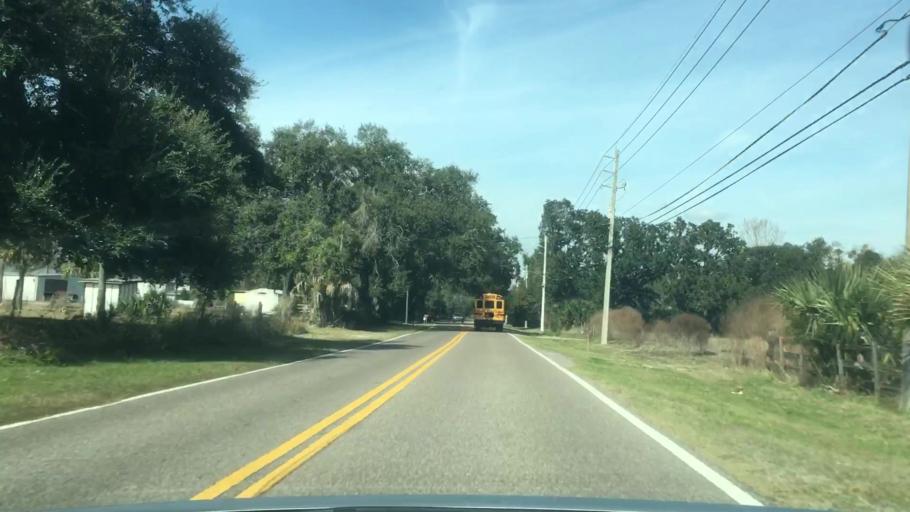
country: US
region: Florida
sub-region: Duval County
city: Jacksonville
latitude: 30.4589
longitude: -81.5594
